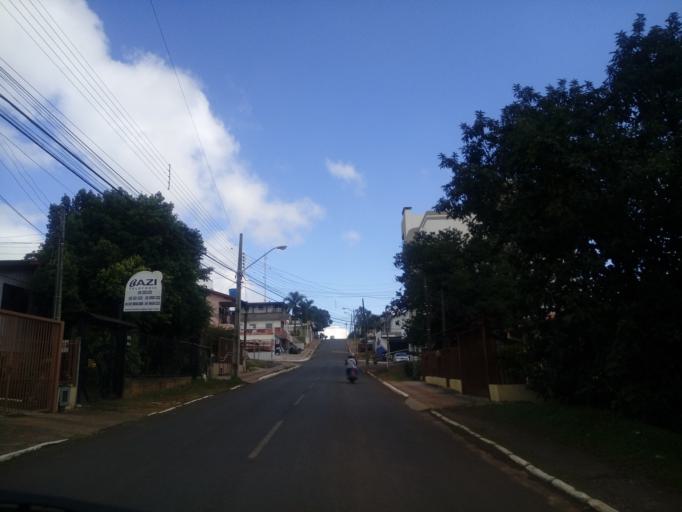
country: BR
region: Santa Catarina
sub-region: Chapeco
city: Chapeco
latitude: -27.1170
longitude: -52.6209
